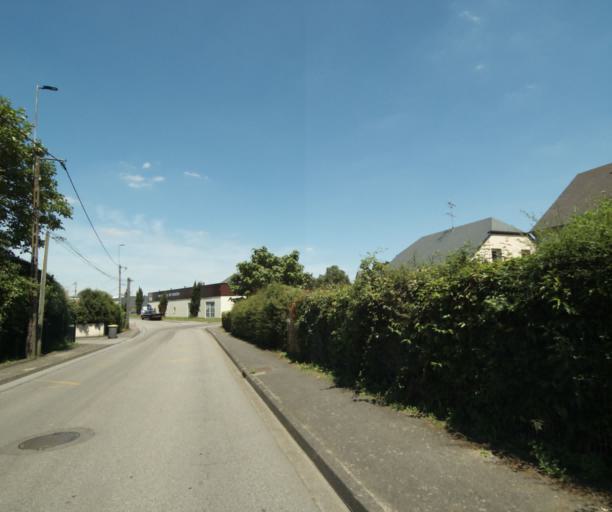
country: FR
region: Pays de la Loire
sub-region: Departement de la Mayenne
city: Laval
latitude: 48.0677
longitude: -0.7949
